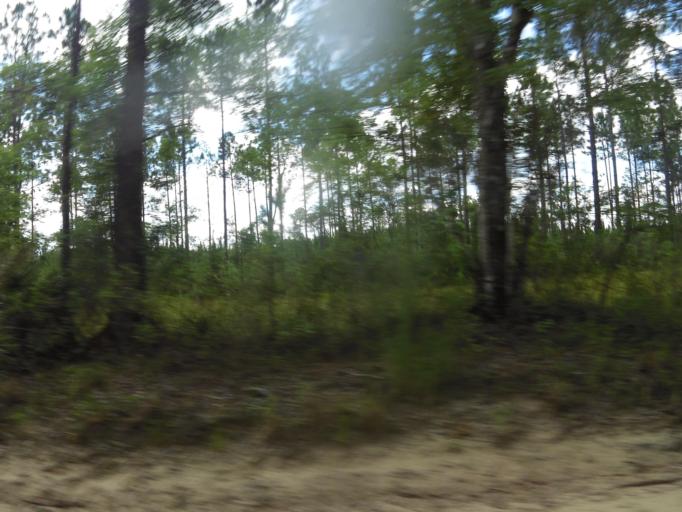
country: US
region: Florida
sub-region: Clay County
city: Asbury Lake
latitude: 29.8935
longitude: -81.8699
